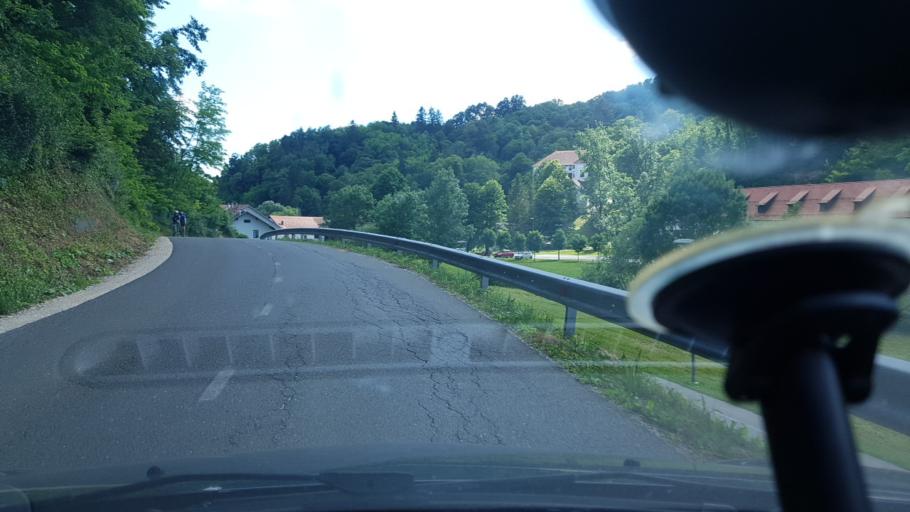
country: SI
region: Rogatec
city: Rogatec
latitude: 46.2312
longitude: 15.6991
